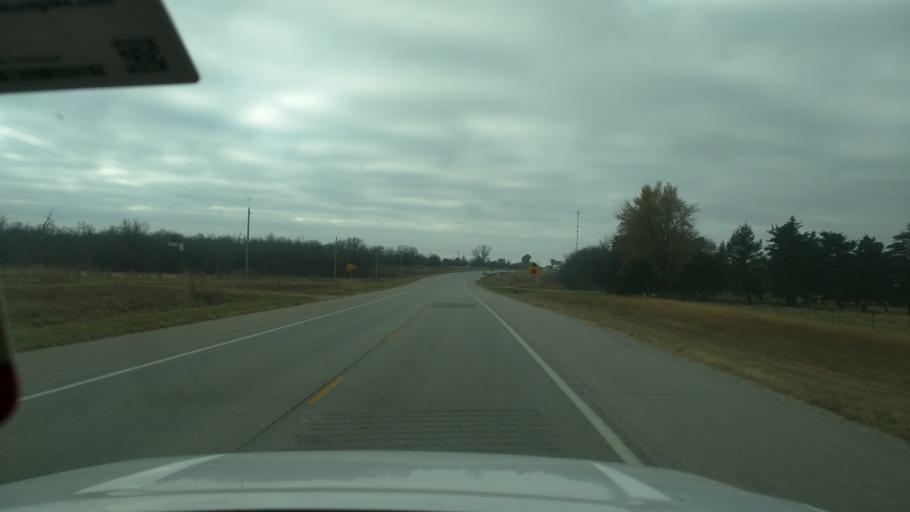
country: US
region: Kansas
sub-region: Elk County
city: Howard
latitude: 37.6411
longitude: -96.2344
